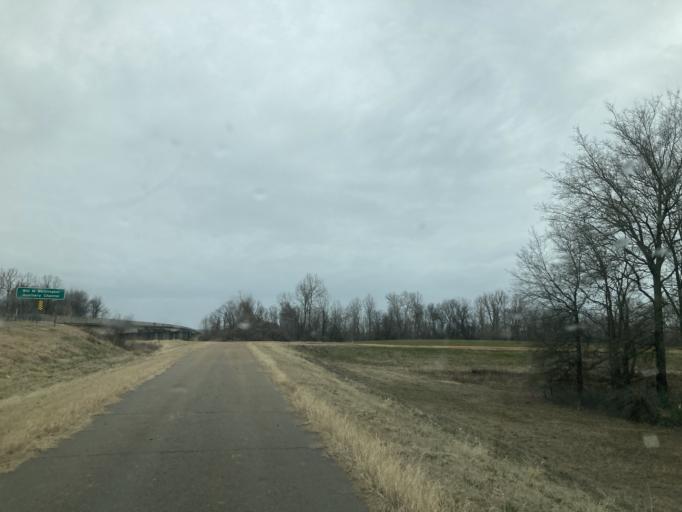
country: US
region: Mississippi
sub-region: Humphreys County
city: Belzoni
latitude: 33.0519
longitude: -90.4677
